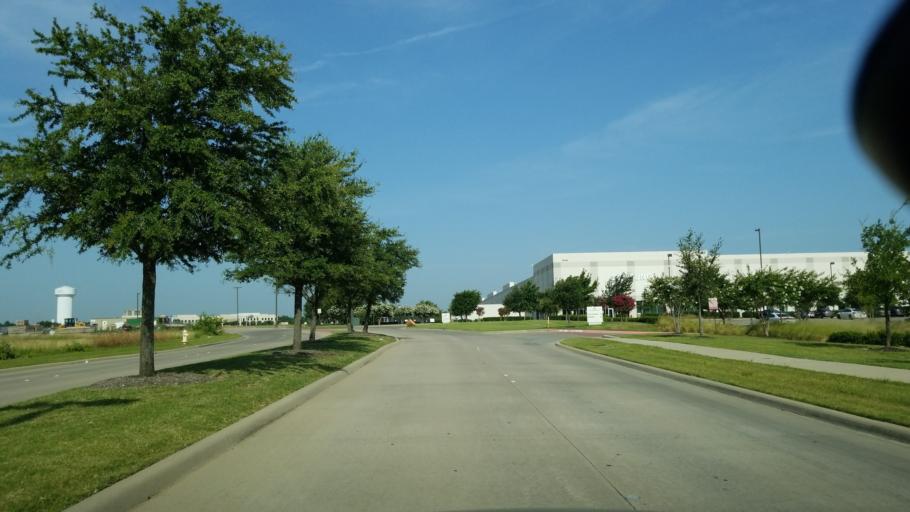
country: US
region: Texas
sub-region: Dallas County
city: Coppell
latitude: 32.9300
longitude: -96.9964
